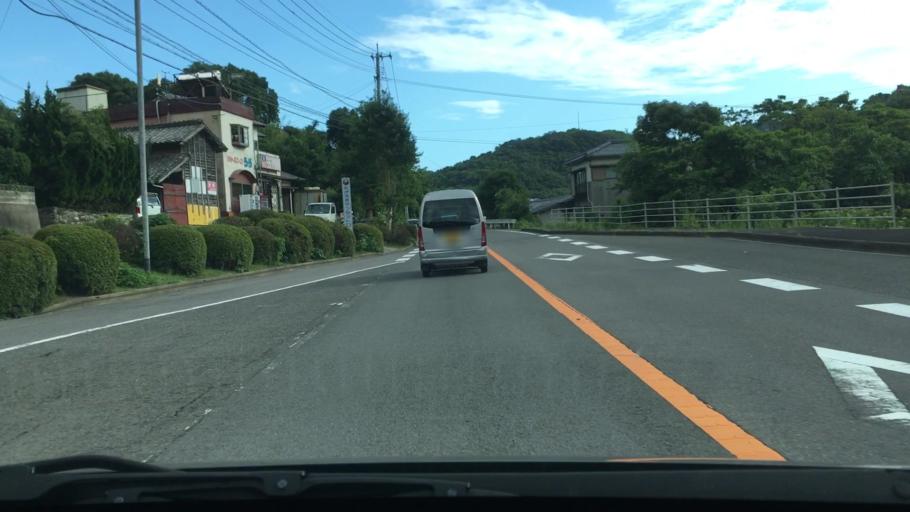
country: JP
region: Nagasaki
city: Togitsu
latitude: 32.8225
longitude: 129.7343
